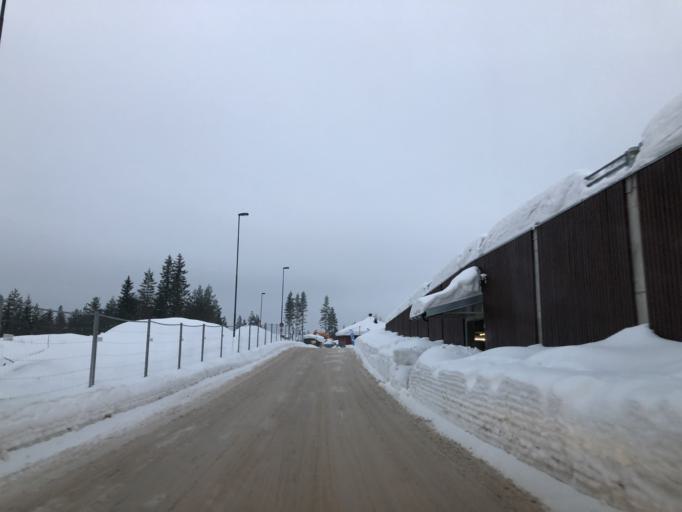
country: NO
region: Hedmark
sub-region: Trysil
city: Innbygda
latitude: 61.3066
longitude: 12.2444
